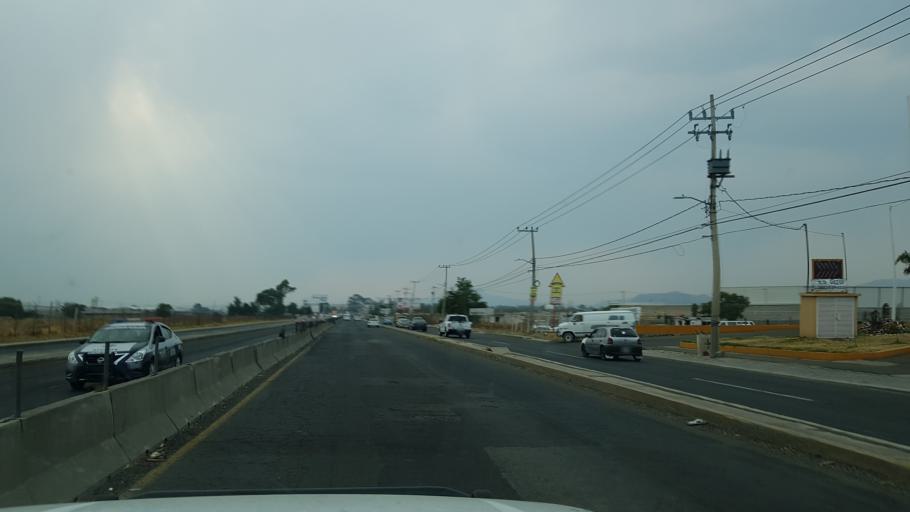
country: MX
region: Mexico
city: Cocotitlan
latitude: 19.2447
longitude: -98.8634
